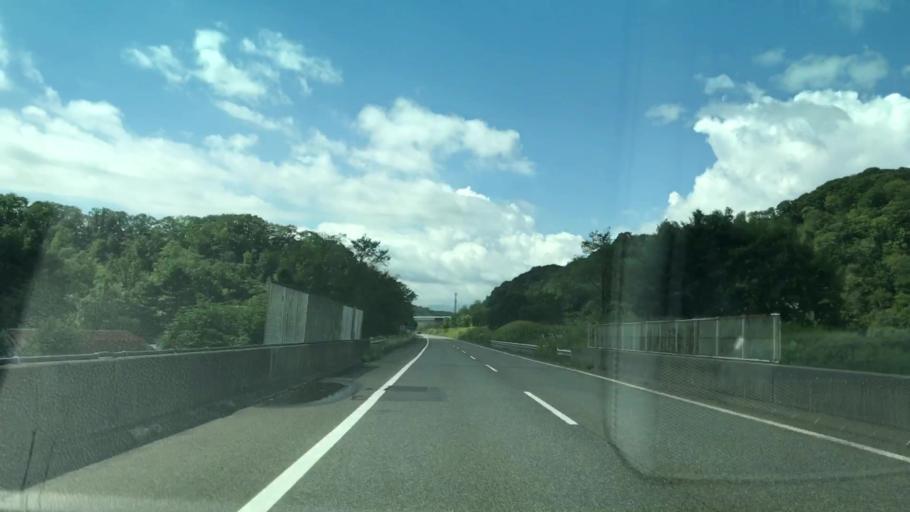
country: JP
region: Hokkaido
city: Shiraoi
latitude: 42.5689
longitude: 141.3422
